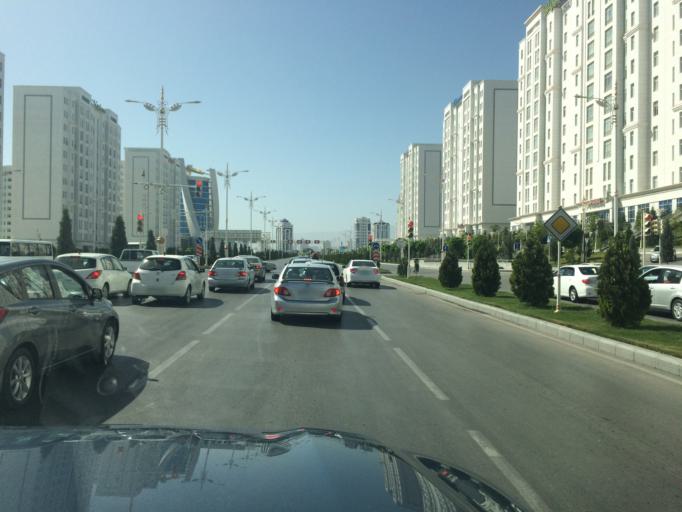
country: TM
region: Ahal
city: Ashgabat
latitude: 37.9343
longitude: 58.3666
